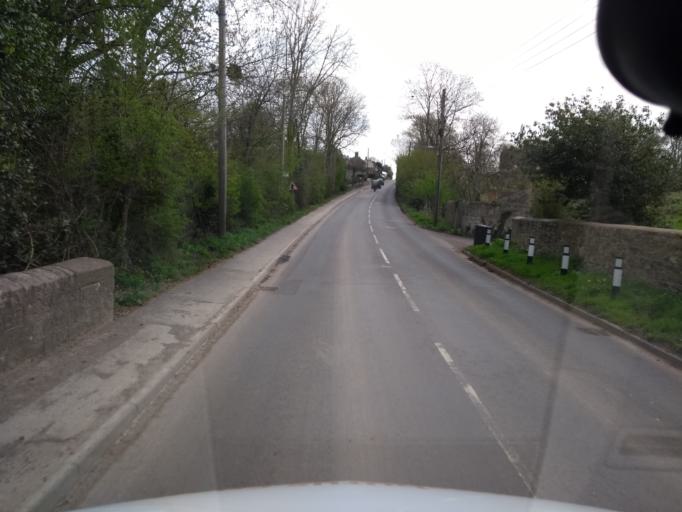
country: GB
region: England
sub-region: Somerset
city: Langport
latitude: 51.0452
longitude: -2.8130
